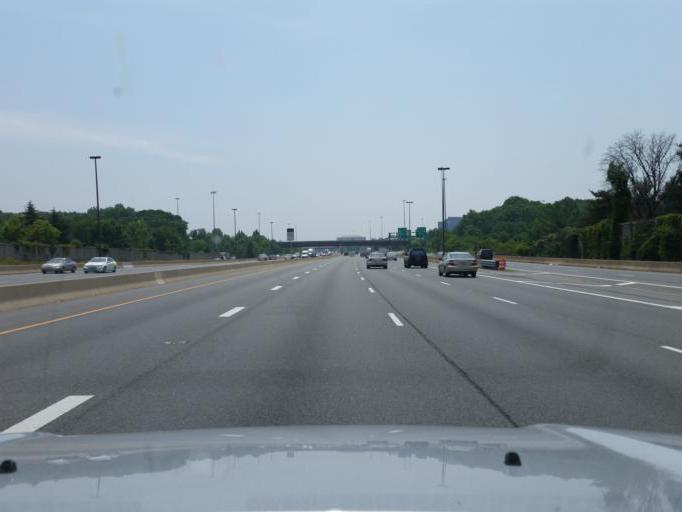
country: US
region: Maryland
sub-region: Montgomery County
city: Gaithersburg
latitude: 39.1261
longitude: -77.2018
